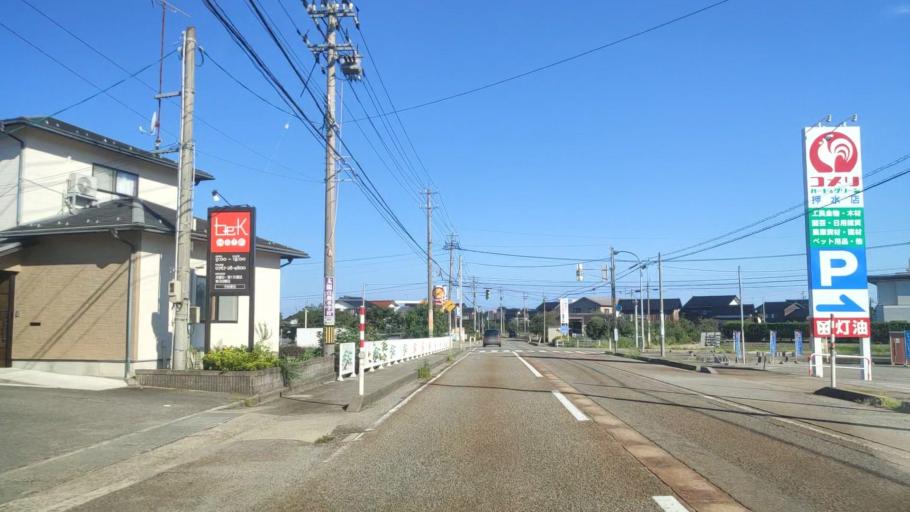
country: JP
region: Ishikawa
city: Hakui
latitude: 36.8202
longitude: 136.7573
